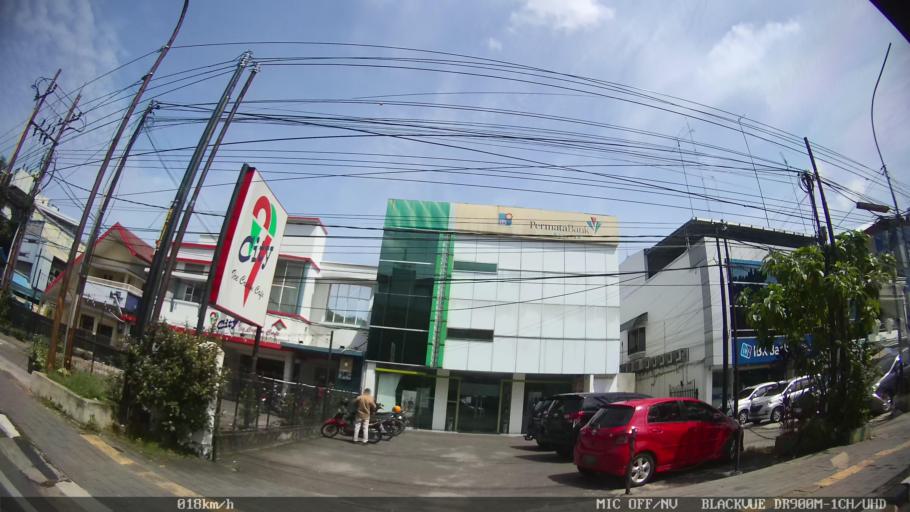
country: ID
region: North Sumatra
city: Medan
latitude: 3.5839
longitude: 98.6754
